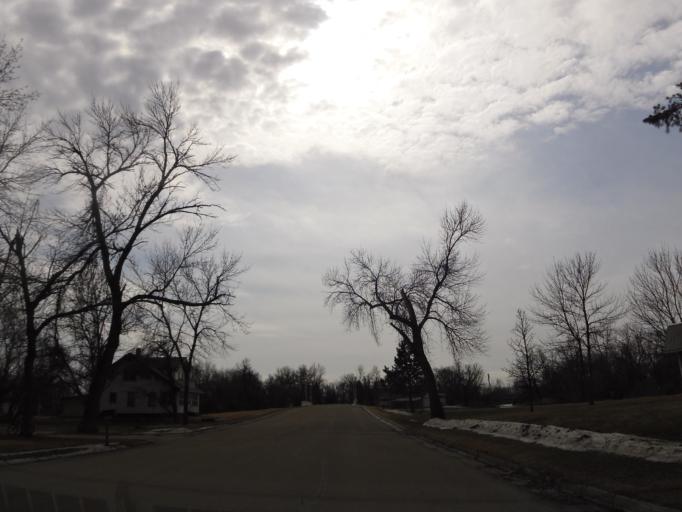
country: US
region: North Dakota
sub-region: Walsh County
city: Grafton
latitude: 48.2869
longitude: -97.3699
